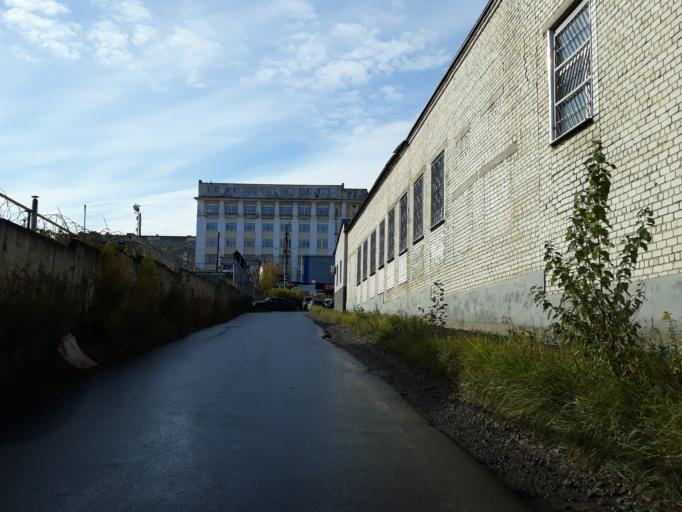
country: RU
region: Nizjnij Novgorod
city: Nizhniy Novgorod
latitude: 56.2499
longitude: 43.9911
